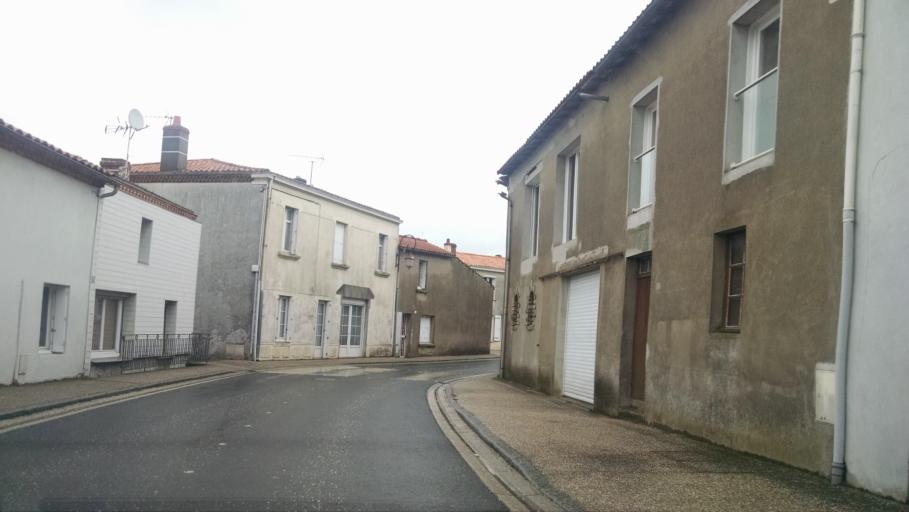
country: FR
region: Pays de la Loire
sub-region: Departement de la Loire-Atlantique
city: Monnieres
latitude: 47.1311
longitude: -1.3564
